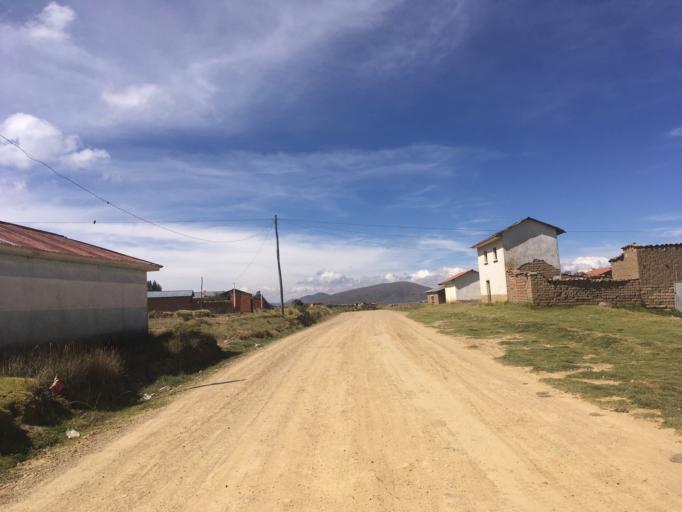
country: BO
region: La Paz
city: San Pedro
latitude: -16.2612
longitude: -68.8756
